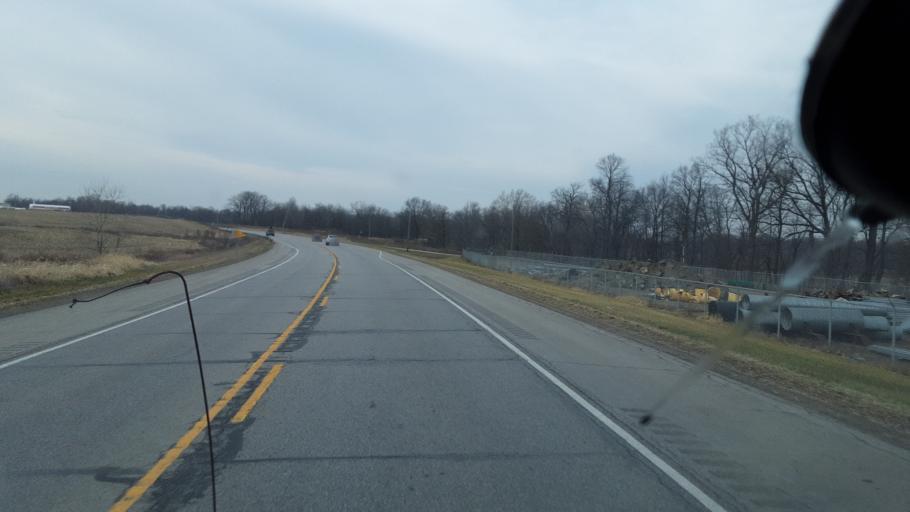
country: US
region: Indiana
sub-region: DeKalb County
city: Waterloo
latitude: 41.4386
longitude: -85.0373
